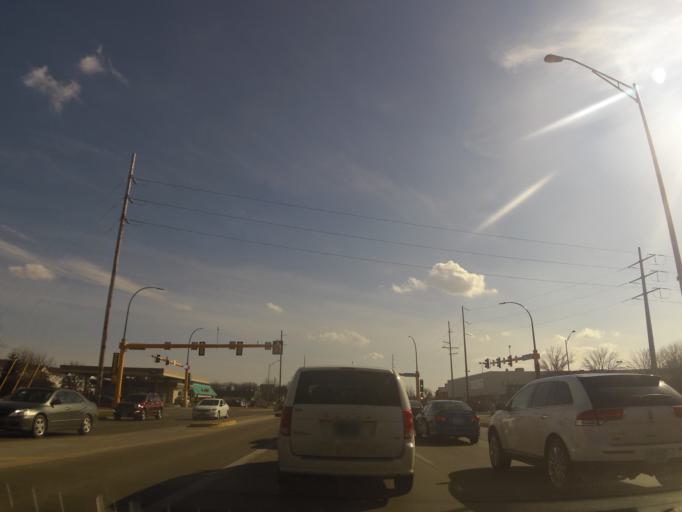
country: US
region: North Dakota
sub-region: Grand Forks County
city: Grand Forks
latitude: 47.8973
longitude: -97.0667
